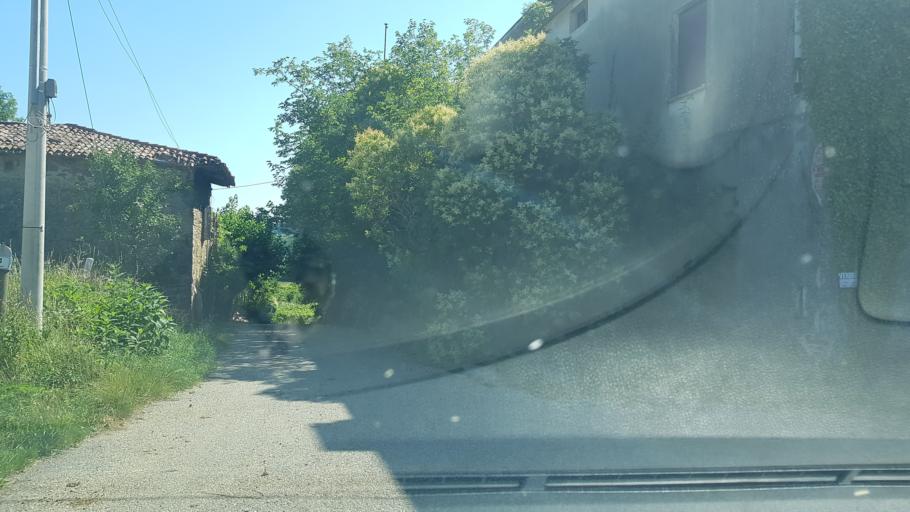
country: SI
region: Brda
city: Dobrovo
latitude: 45.9728
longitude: 13.5143
